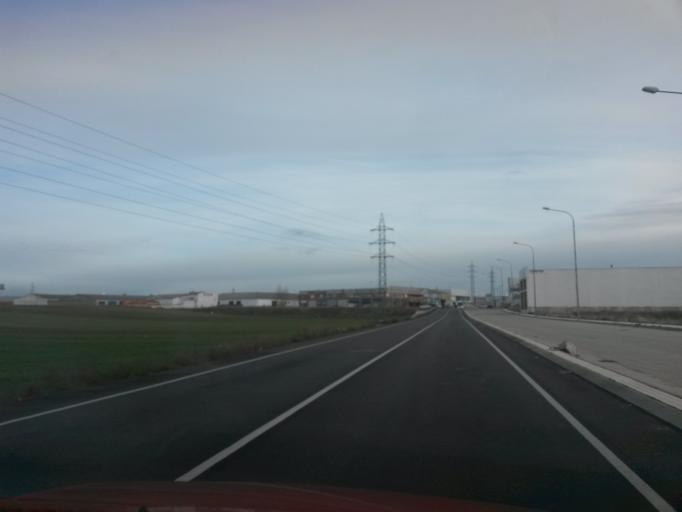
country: ES
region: Castille and Leon
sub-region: Provincia de Salamanca
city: Villares de la Reina
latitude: 40.9976
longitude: -5.6371
